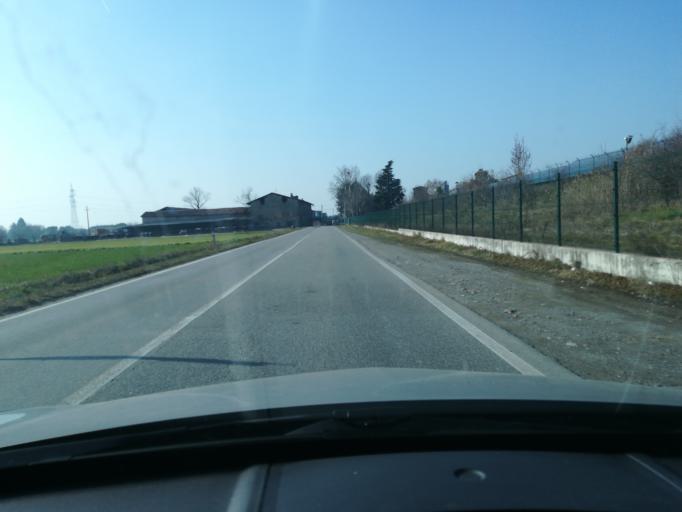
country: IT
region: Lombardy
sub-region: Provincia di Bergamo
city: Zanica
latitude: 45.6470
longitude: 9.7012
